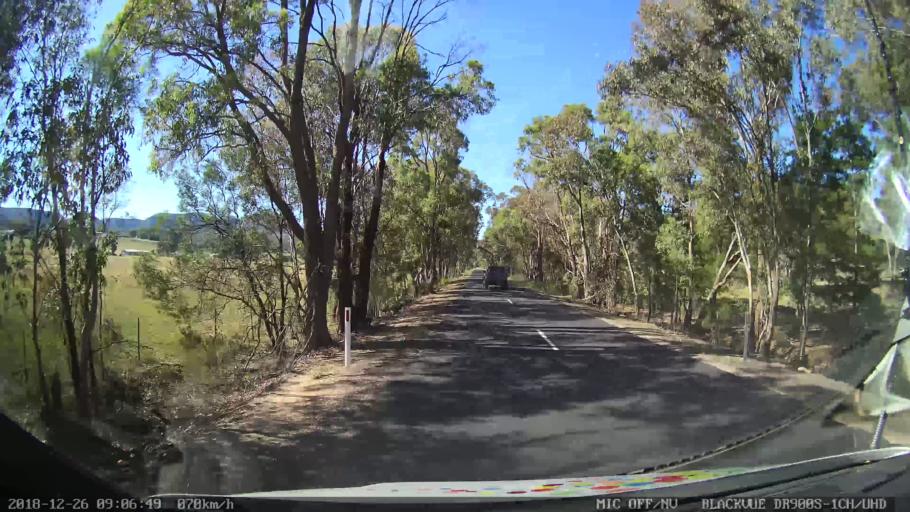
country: AU
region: New South Wales
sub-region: Mid-Western Regional
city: Kandos
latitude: -32.6986
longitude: 150.0056
